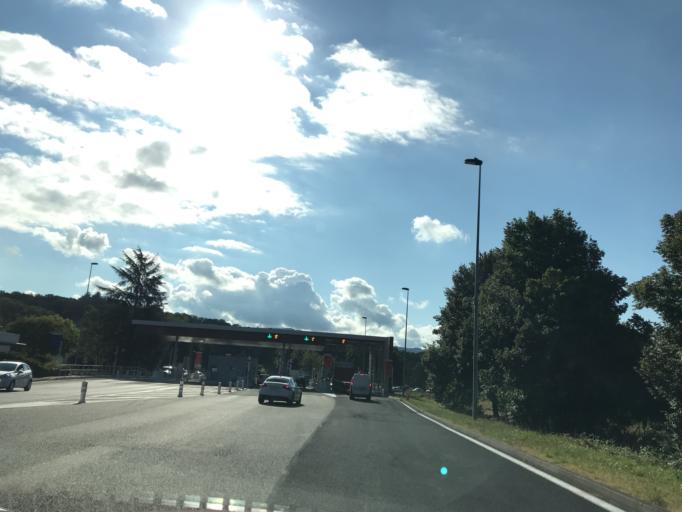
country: FR
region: Auvergne
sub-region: Departement du Puy-de-Dome
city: Peschadoires
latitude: 45.8602
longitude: 3.5026
